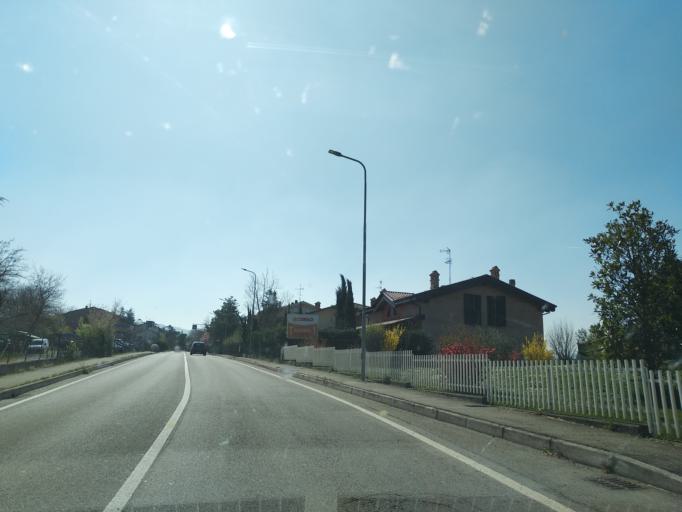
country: IT
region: Emilia-Romagna
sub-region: Provincia di Reggio Emilia
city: Albinea
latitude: 44.6361
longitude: 10.6060
